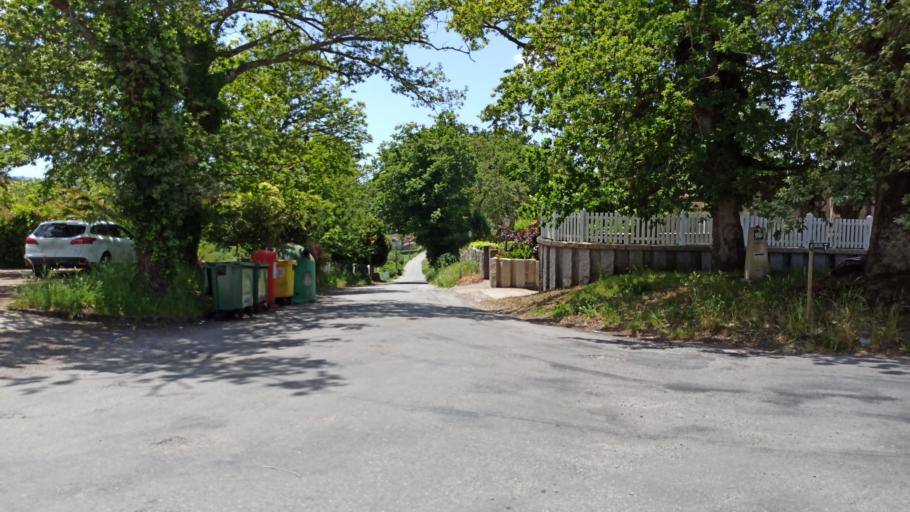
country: ES
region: Galicia
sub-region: Provincia da Coruna
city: Negreira
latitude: 42.9089
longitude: -8.7288
